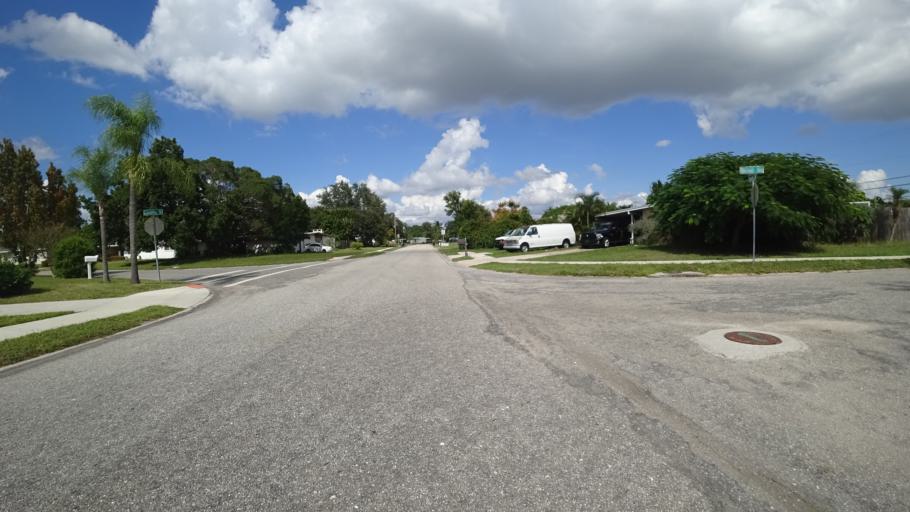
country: US
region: Florida
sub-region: Manatee County
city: Bayshore Gardens
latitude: 27.4264
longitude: -82.5847
